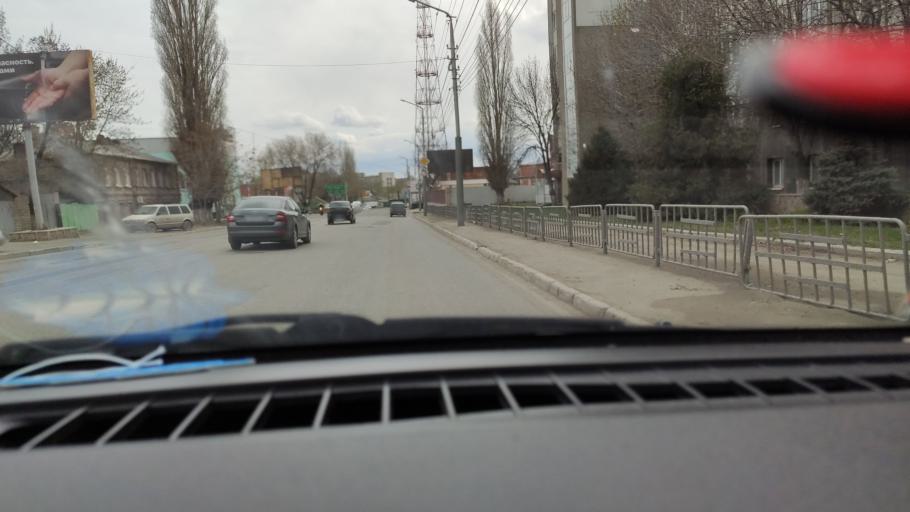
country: RU
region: Saratov
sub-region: Saratovskiy Rayon
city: Saratov
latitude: 51.5494
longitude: 46.0117
